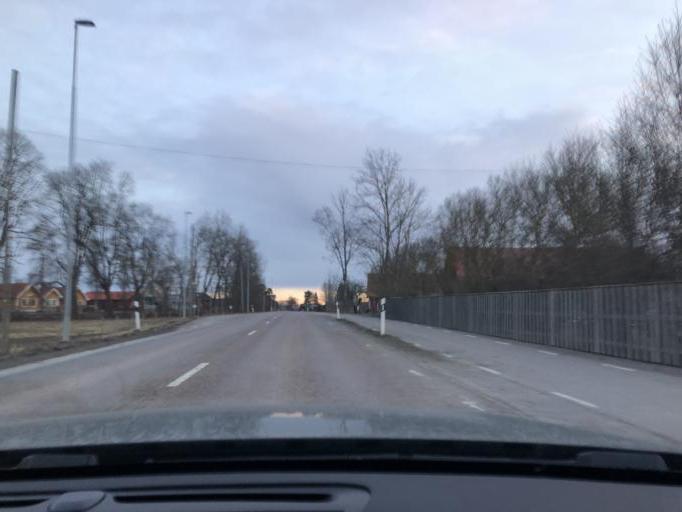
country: SE
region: Uppsala
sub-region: Uppsala Kommun
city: Gamla Uppsala
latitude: 59.9141
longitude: 17.6429
